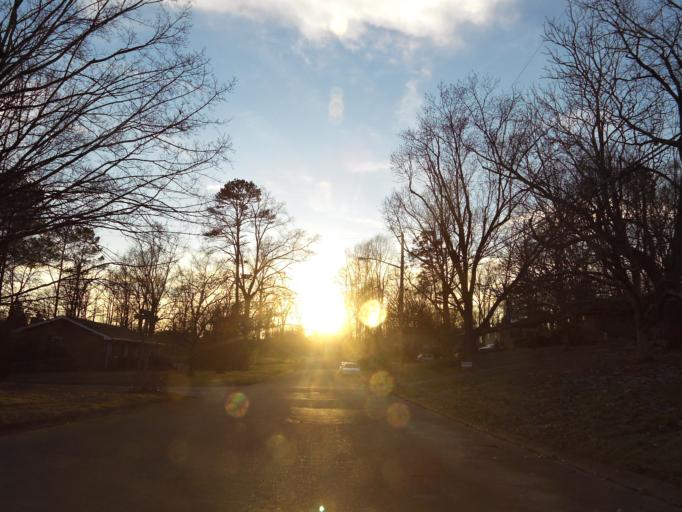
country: US
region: Tennessee
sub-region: Knox County
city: Knoxville
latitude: 36.0161
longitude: -83.8715
